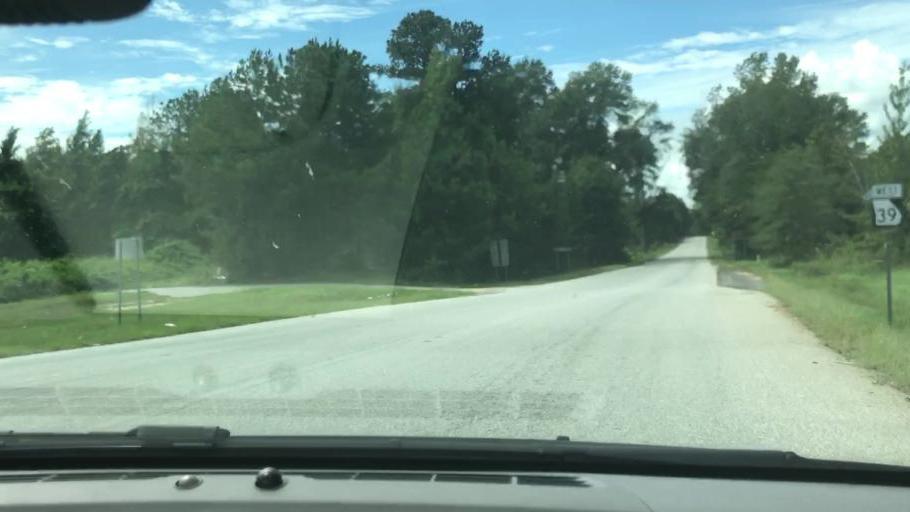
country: US
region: Georgia
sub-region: Stewart County
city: Lumpkin
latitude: 32.1483
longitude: -84.8279
